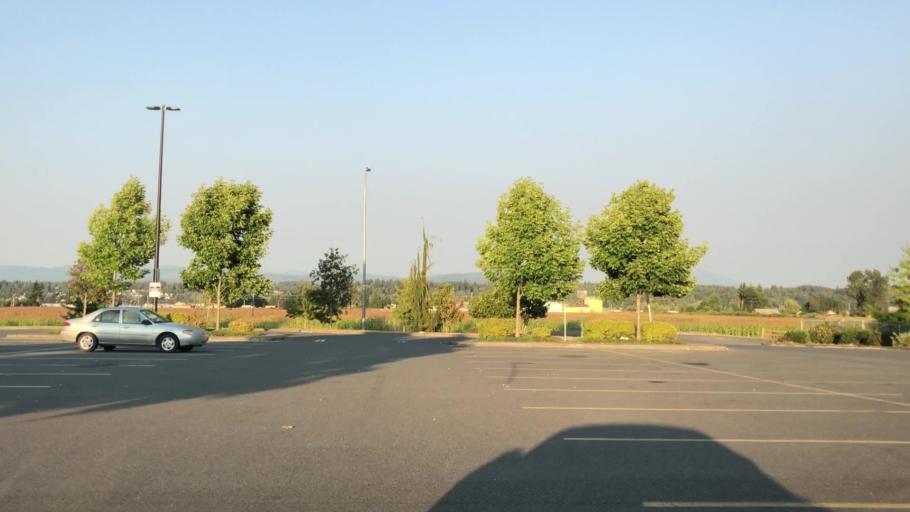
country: US
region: Washington
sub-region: Snohomish County
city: Smokey Point
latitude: 48.1497
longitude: -122.1733
